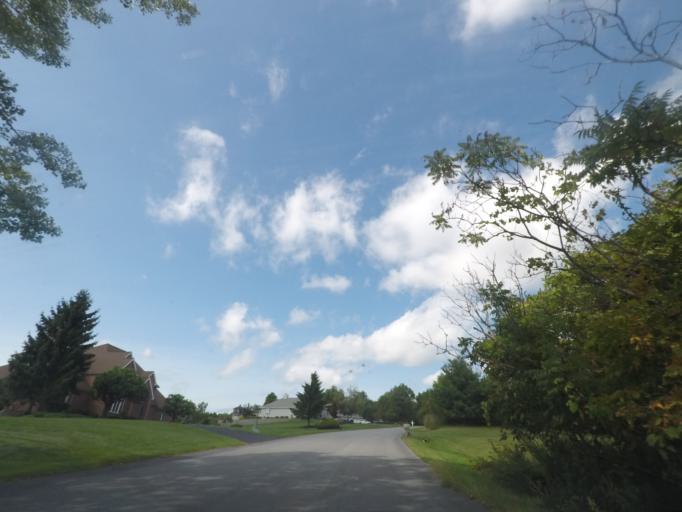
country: US
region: New York
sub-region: Rensselaer County
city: West Sand Lake
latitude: 42.5933
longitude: -73.6251
